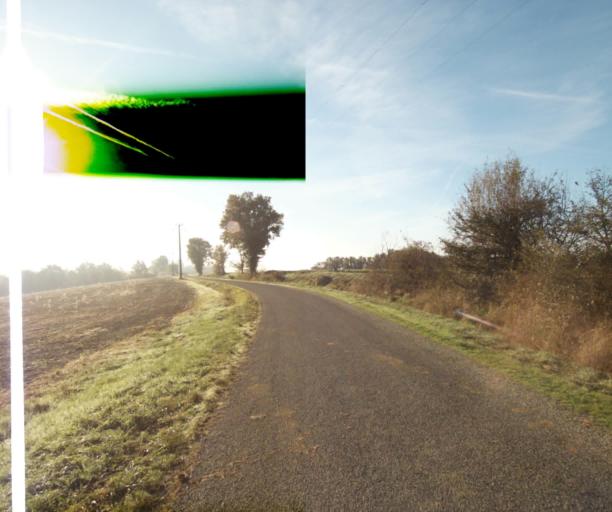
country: FR
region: Midi-Pyrenees
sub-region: Departement de la Haute-Garonne
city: Villemur-sur-Tarn
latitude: 43.8991
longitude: 1.4776
